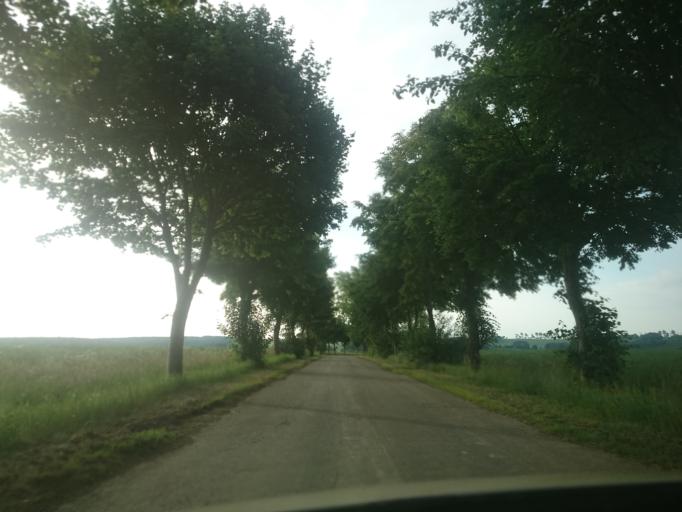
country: DE
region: Saxony
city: Eppendorf
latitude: 50.8344
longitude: 13.2300
